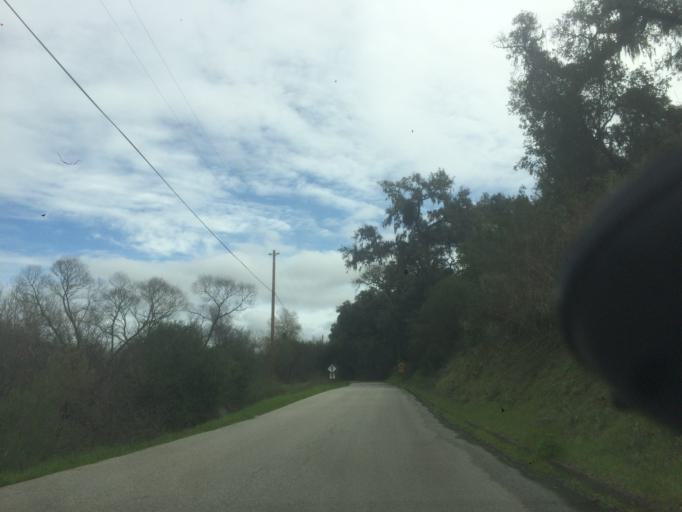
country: US
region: California
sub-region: San Luis Obispo County
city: Nipomo
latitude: 35.2072
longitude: -120.4132
